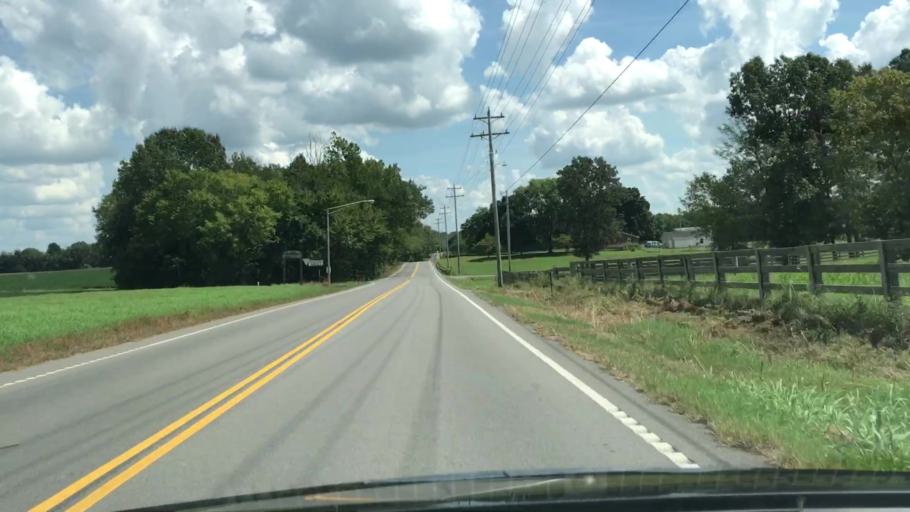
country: US
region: Tennessee
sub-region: Robertson County
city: Cross Plains
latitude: 36.5508
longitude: -86.7273
